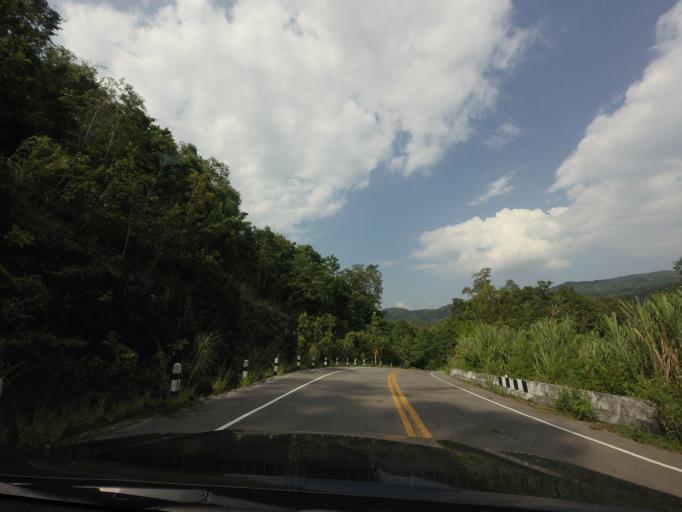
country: TH
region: Nan
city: Na Noi
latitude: 18.2891
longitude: 100.9283
